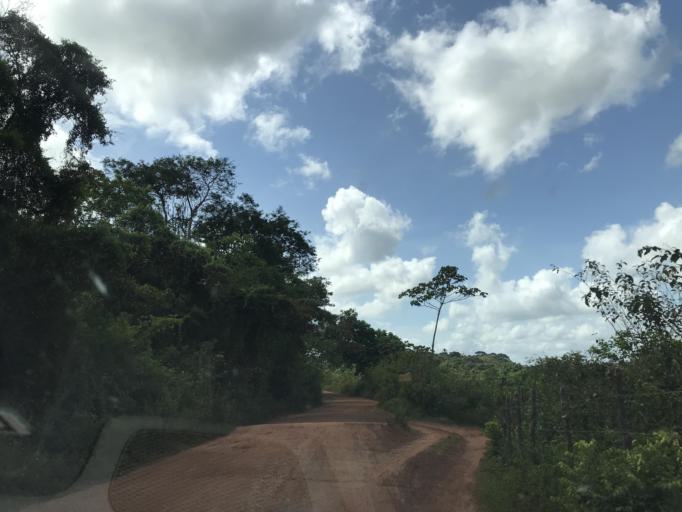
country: BR
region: Bahia
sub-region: Entre Rios
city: Entre Rios
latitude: -12.1634
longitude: -38.0751
